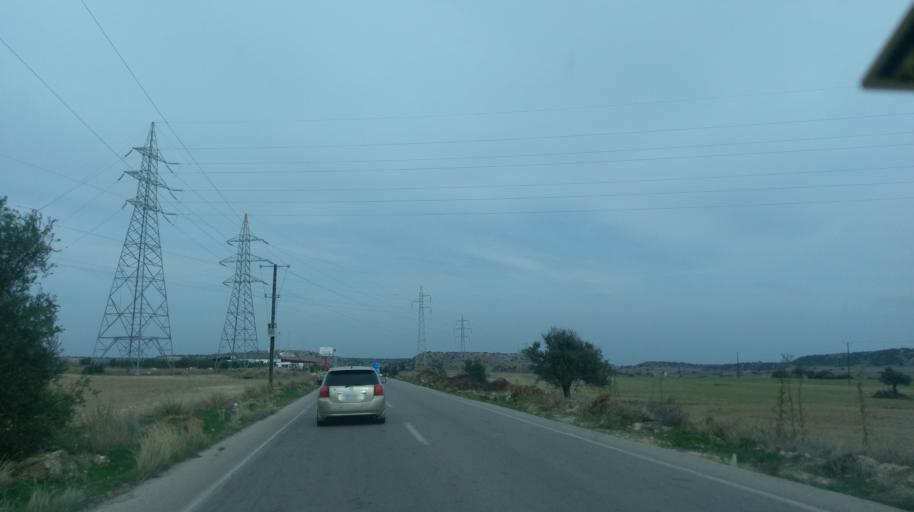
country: CY
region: Ammochostos
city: Leonarisso
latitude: 35.3791
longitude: 34.0387
